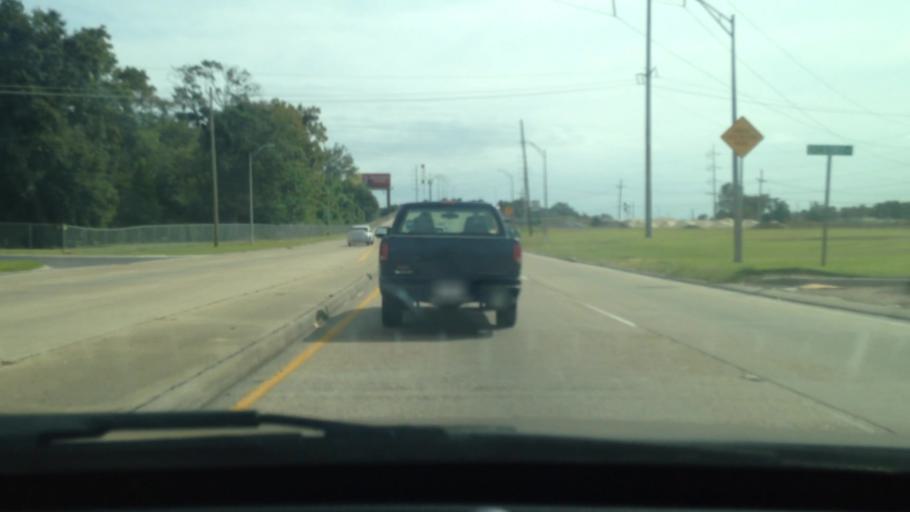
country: US
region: Louisiana
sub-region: Jefferson Parish
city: River Ridge
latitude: 29.9755
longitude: -90.2094
